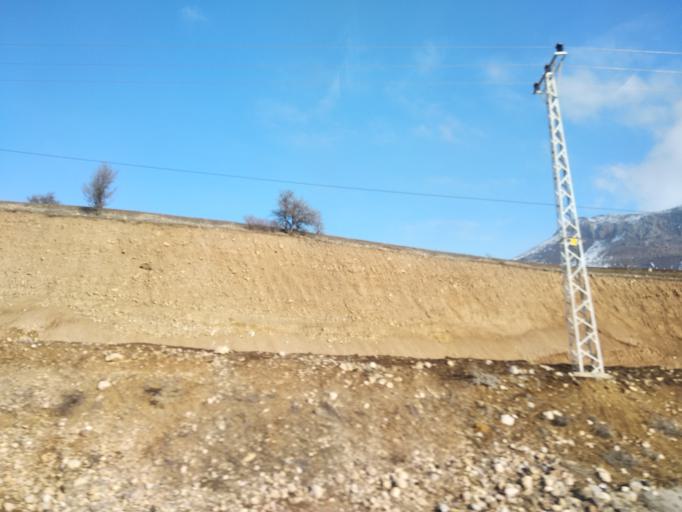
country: TR
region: Gumushane
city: Kelkit
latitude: 40.0130
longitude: 39.5308
